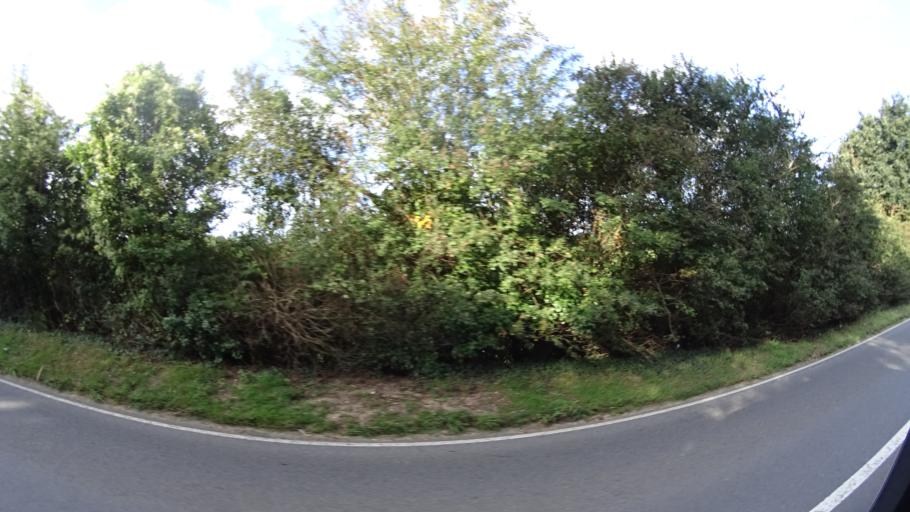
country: GB
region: England
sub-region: Dorset
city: Lytchett Matravers
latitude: 50.7711
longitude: -2.0667
